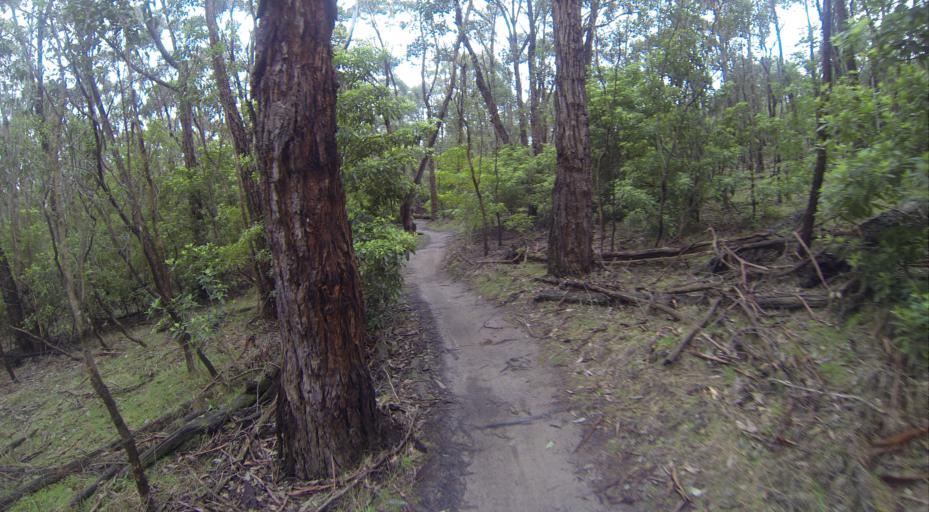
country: AU
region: Victoria
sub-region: Yarra Ranges
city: Lysterfield
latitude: -37.9408
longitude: 145.3031
